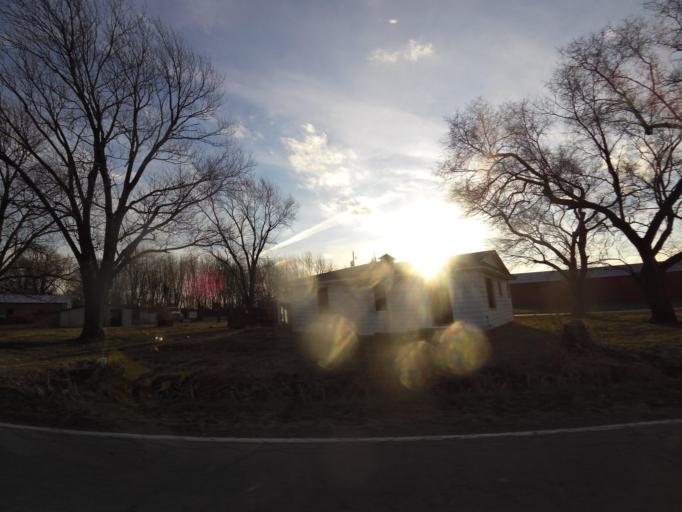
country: US
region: Illinois
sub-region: Fayette County
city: Vandalia
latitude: 38.9414
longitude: -89.1716
